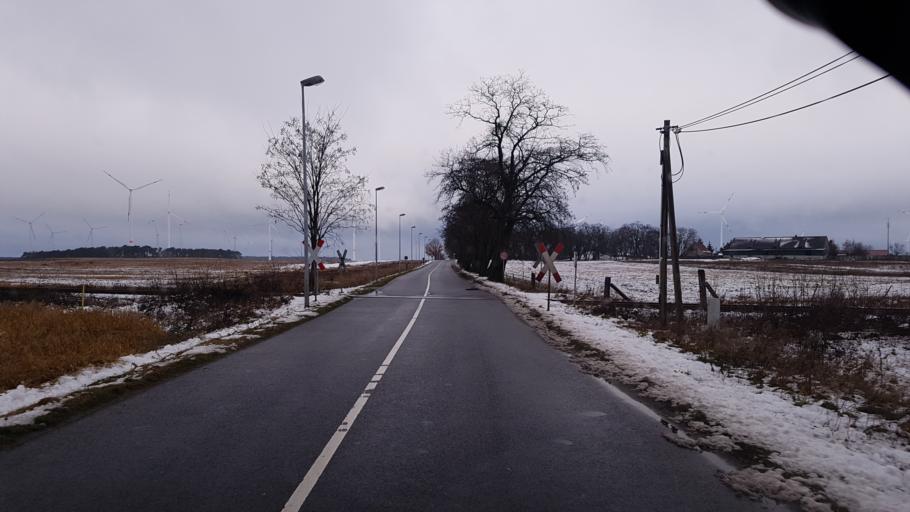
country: DE
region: Brandenburg
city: Luckau
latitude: 51.8807
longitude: 13.7930
